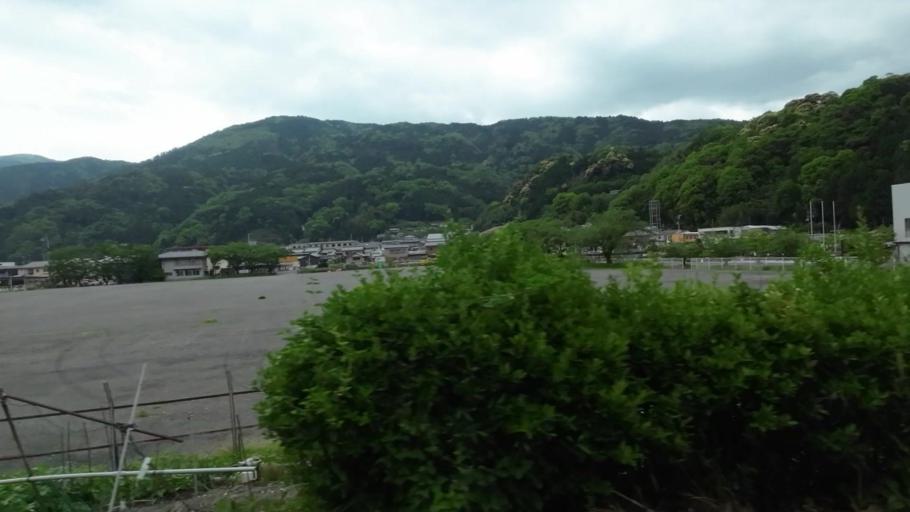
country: JP
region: Tokushima
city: Ikedacho
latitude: 34.0290
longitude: 133.7998
